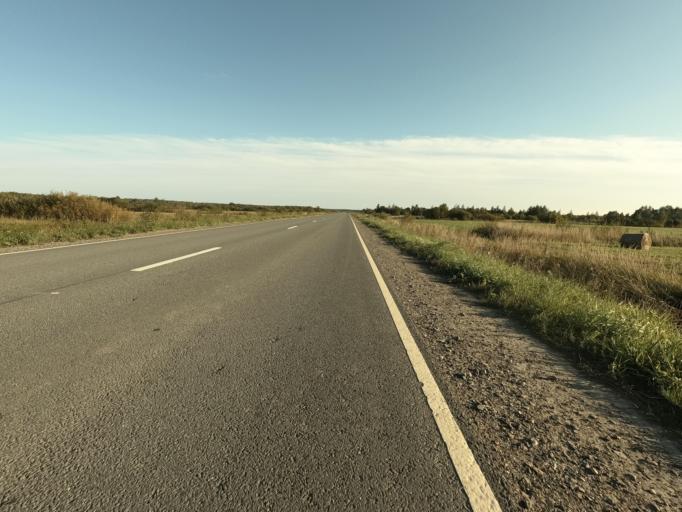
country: RU
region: St.-Petersburg
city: Sapernyy
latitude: 59.7485
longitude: 30.6410
